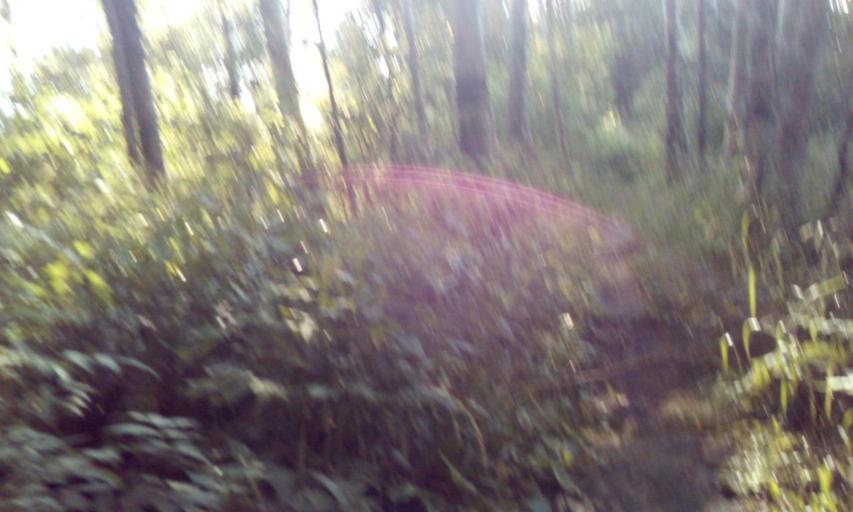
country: RU
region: Moskovskaya
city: Kievskij
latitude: 55.3511
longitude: 36.9158
